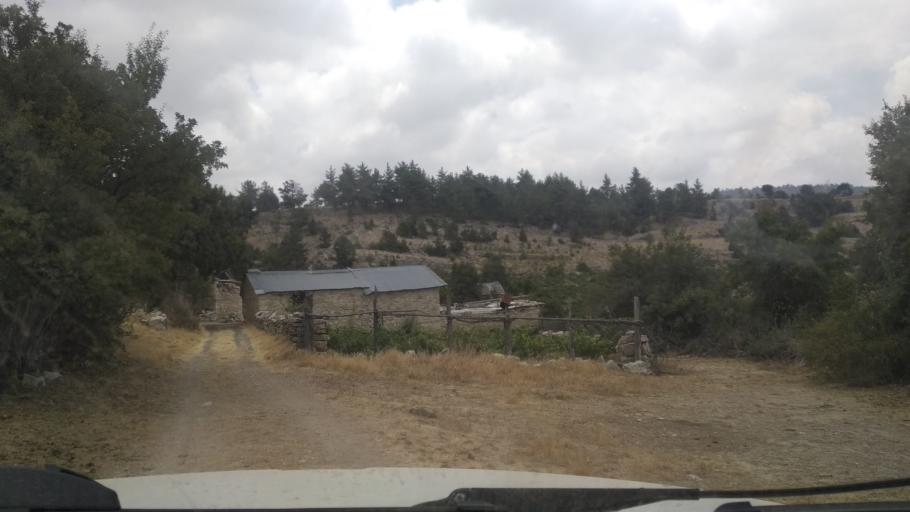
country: TR
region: Mersin
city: Sarikavak
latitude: 36.5984
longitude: 33.7280
